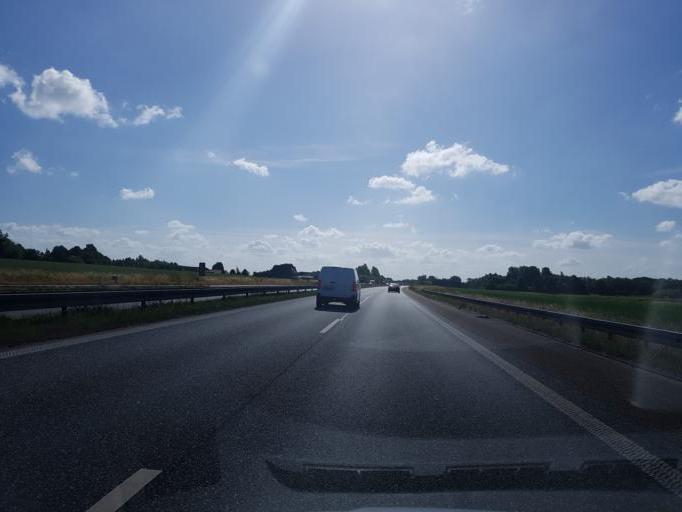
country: DK
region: Zealand
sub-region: Soro Kommune
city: Frederiksberg
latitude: 55.4534
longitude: 11.6106
